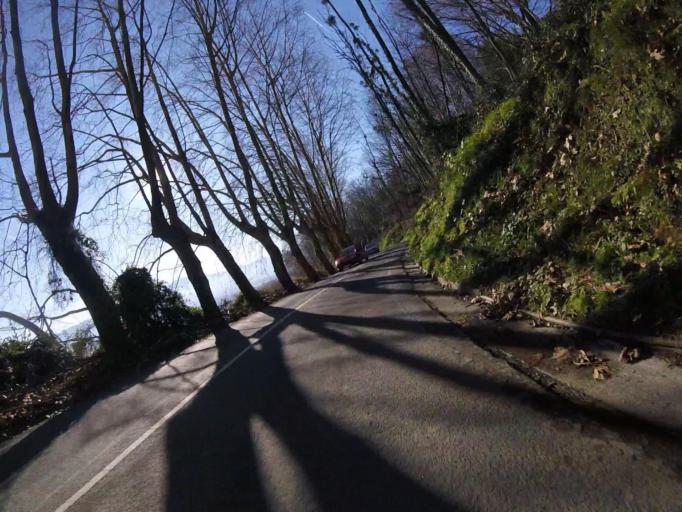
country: ES
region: Basque Country
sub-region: Provincia de Guipuzcoa
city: Fuenterrabia
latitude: 43.3696
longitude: -1.8095
